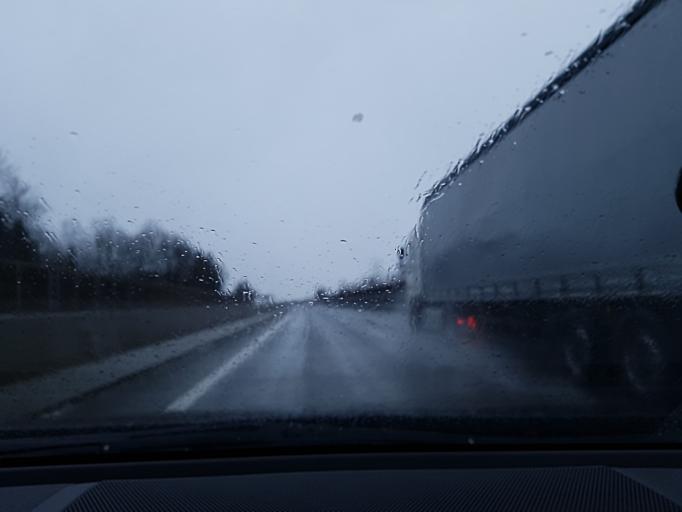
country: AT
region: Salzburg
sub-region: Politischer Bezirk Hallein
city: Golling an der Salzach
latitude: 47.6010
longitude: 13.1500
